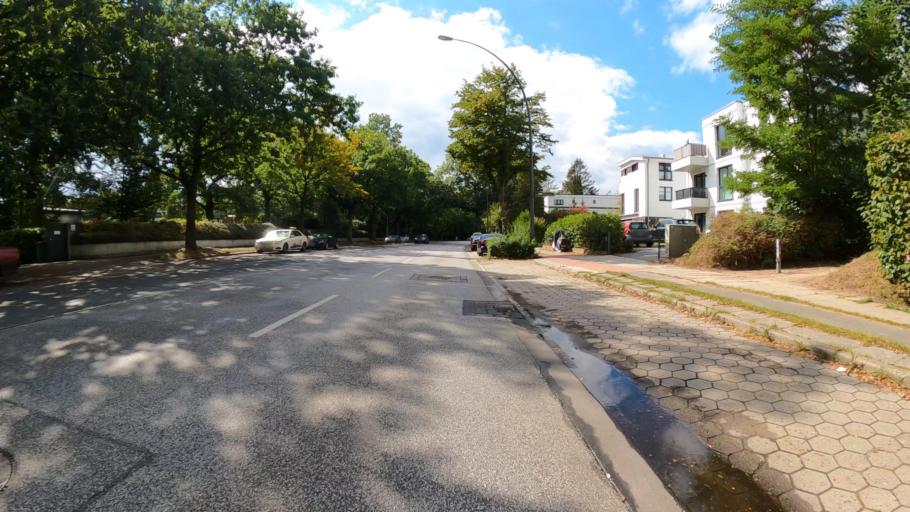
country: DE
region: Hamburg
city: Wellingsbuettel
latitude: 53.6447
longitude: 10.0699
